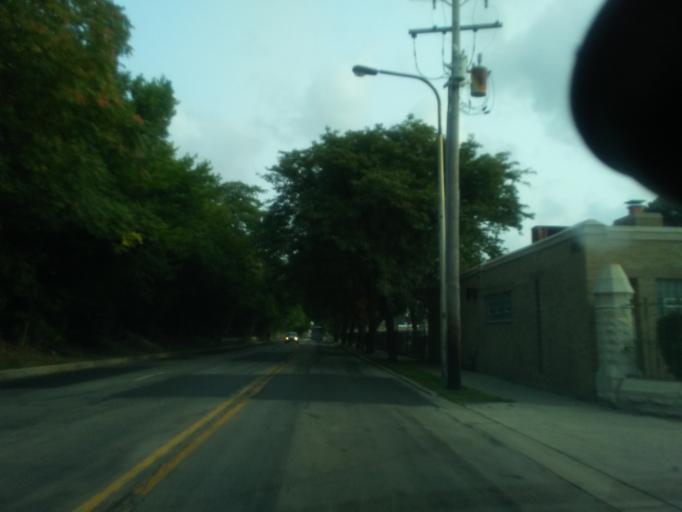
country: US
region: Illinois
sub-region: Cook County
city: Evanston
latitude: 42.0249
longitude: -87.6776
